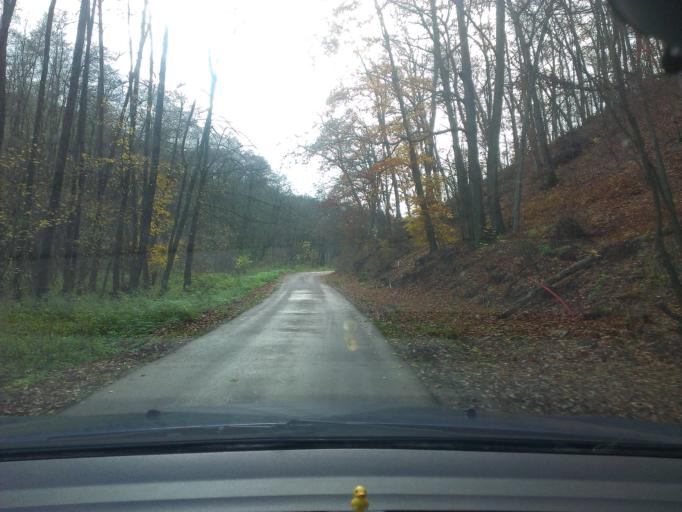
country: SK
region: Trnavsky
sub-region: Okres Trnava
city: Piestany
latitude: 48.6097
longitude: 17.9106
